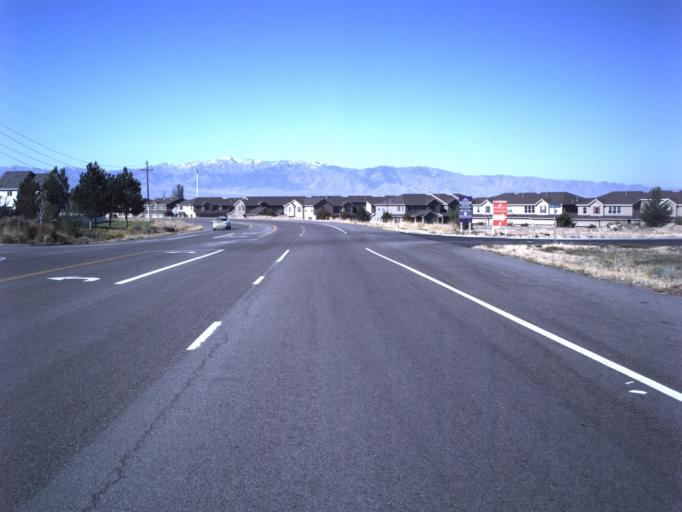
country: US
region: Utah
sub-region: Tooele County
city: Stansbury park
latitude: 40.6532
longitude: -112.2906
